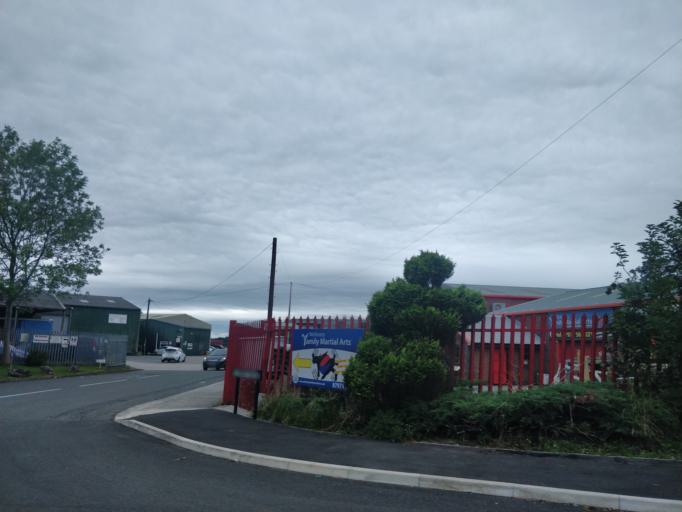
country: GB
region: England
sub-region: Lancashire
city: Ormskirk
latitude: 53.5910
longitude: -2.8630
